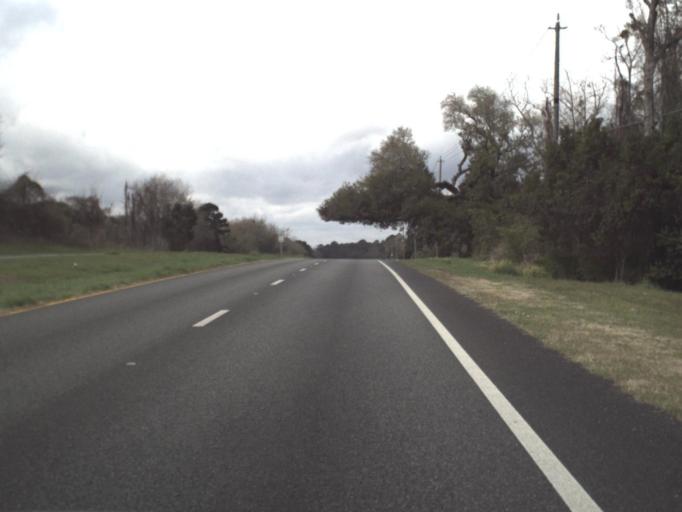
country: US
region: Florida
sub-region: Leon County
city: Tallahassee
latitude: 30.4265
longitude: -84.1840
